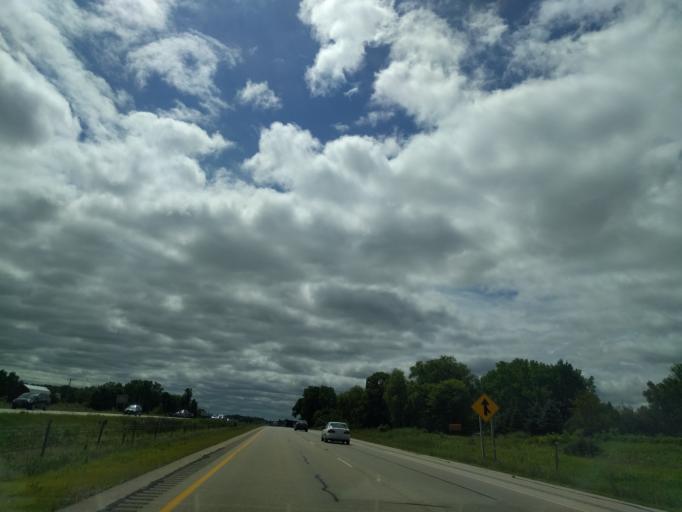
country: US
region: Wisconsin
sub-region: Brown County
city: Suamico
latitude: 44.6754
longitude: -88.0504
